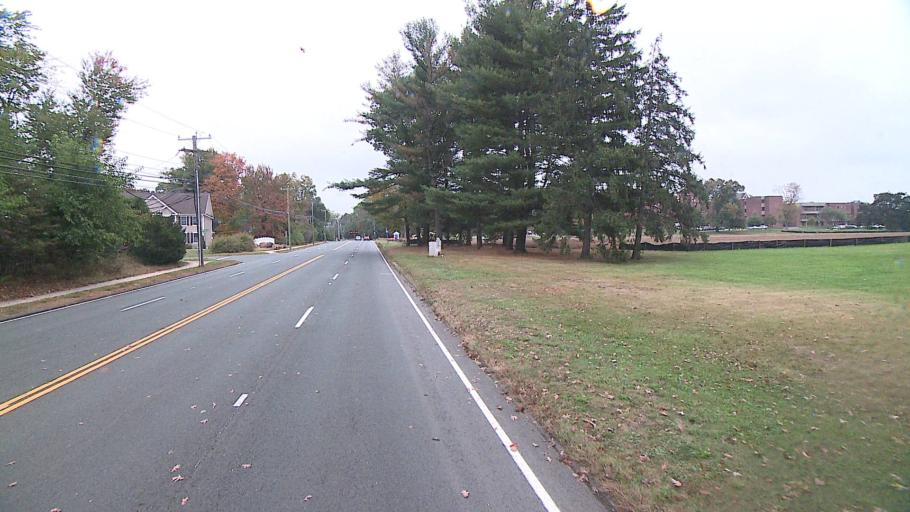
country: US
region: Connecticut
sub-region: Hartford County
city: West Hartford
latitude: 41.7861
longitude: -72.7280
